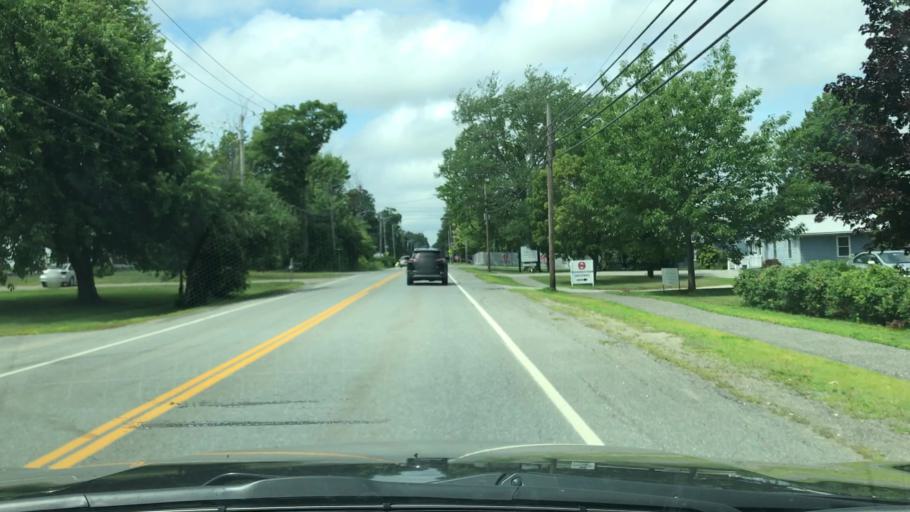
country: US
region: Maine
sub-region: Waldo County
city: Belfast
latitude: 44.4109
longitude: -68.9940
